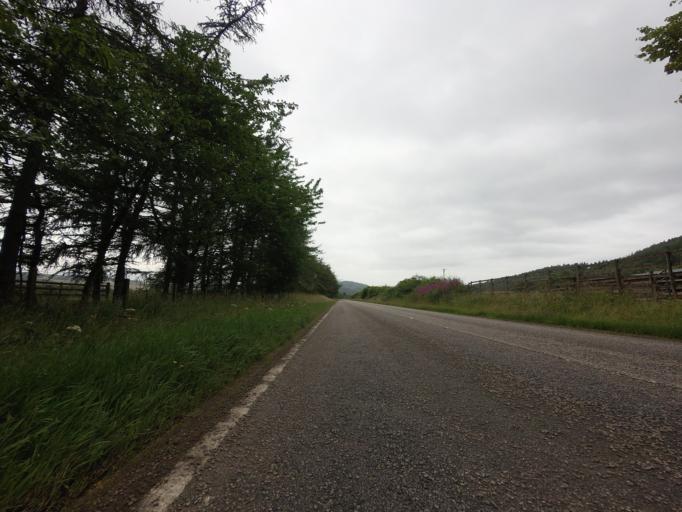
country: GB
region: Scotland
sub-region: Highland
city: Alness
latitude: 57.9148
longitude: -4.3850
